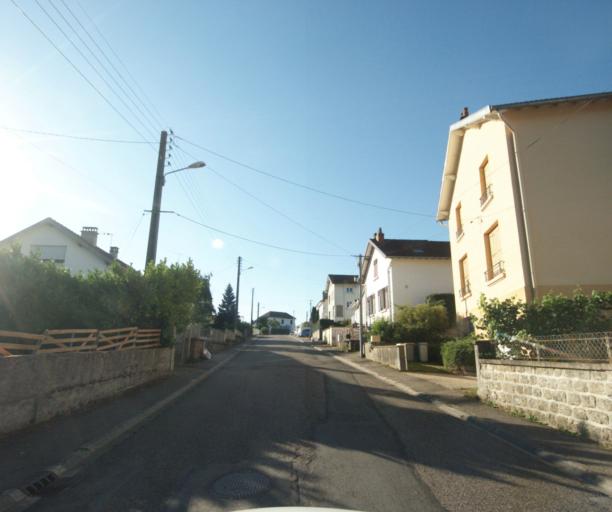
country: FR
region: Lorraine
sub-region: Departement des Vosges
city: Chantraine
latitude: 48.1467
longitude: 6.4601
